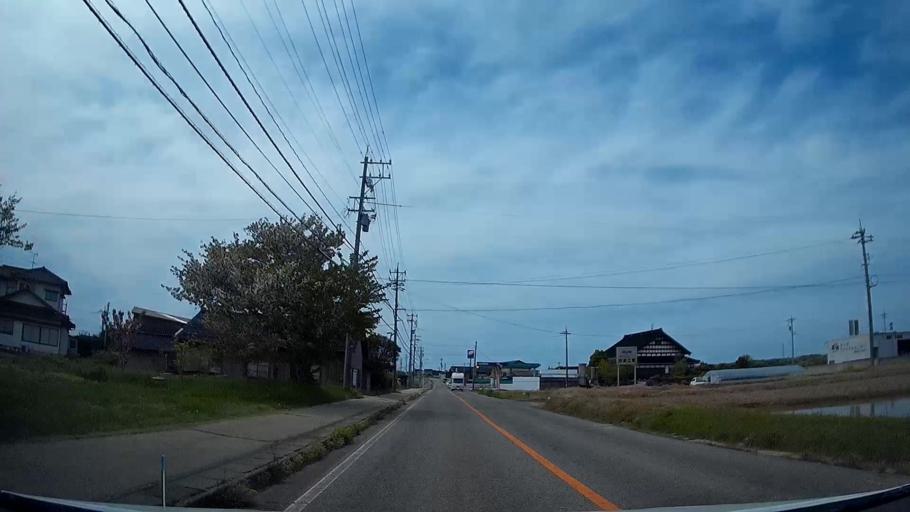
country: JP
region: Ishikawa
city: Hakui
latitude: 37.0091
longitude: 136.7645
